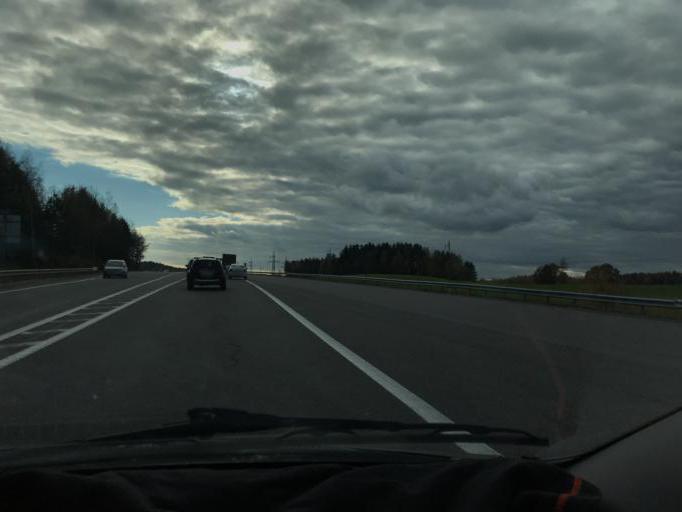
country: BY
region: Minsk
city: Lahoysk
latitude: 54.2126
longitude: 27.8267
